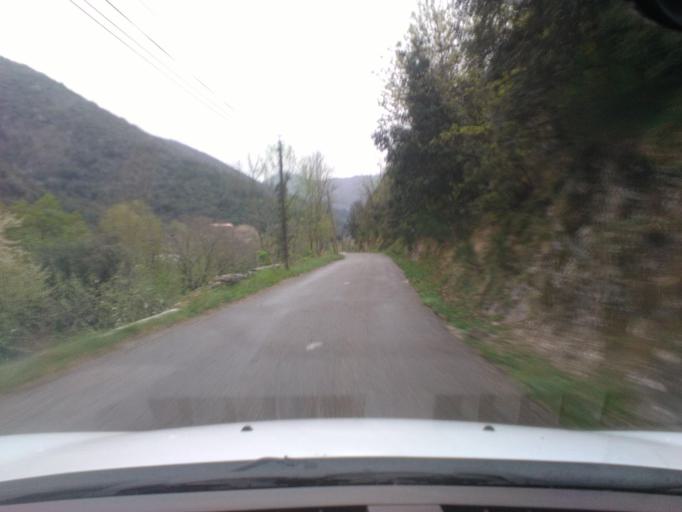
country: FR
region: Languedoc-Roussillon
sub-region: Departement du Gard
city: Valleraugue
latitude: 44.0970
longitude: 3.6325
